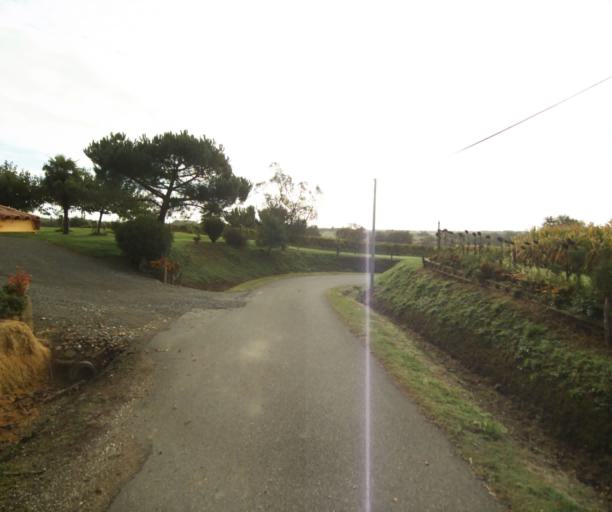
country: FR
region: Midi-Pyrenees
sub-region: Departement du Gers
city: Nogaro
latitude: 43.8120
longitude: -0.0567
